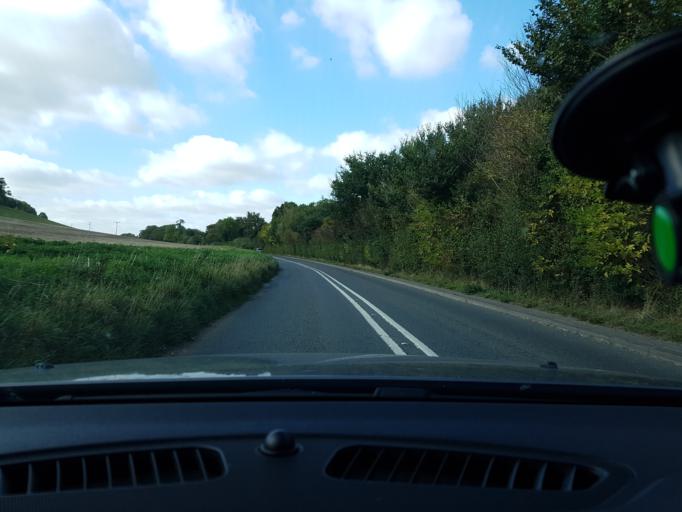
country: GB
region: England
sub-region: West Berkshire
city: Hungerford
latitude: 51.4234
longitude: -1.5226
